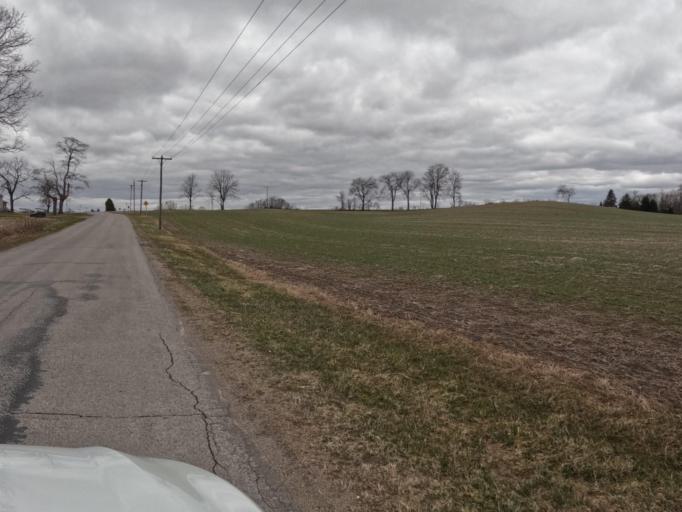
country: CA
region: Ontario
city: Norfolk County
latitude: 42.9552
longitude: -80.3942
